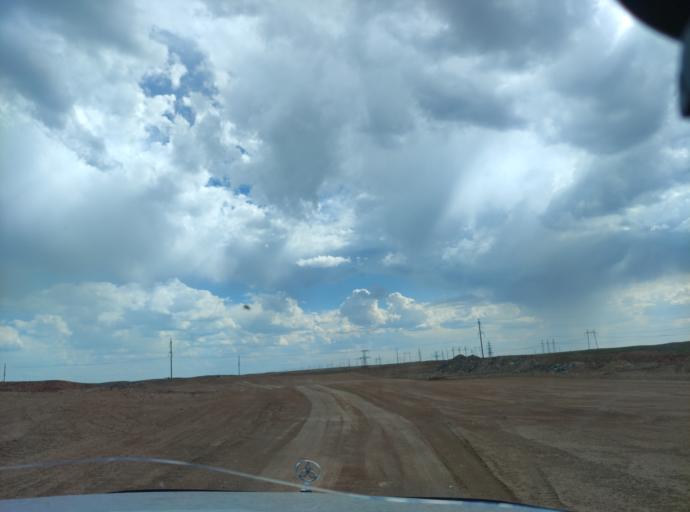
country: KZ
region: Qaraghandy
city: Saryshaghan
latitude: 46.1252
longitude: 73.5964
